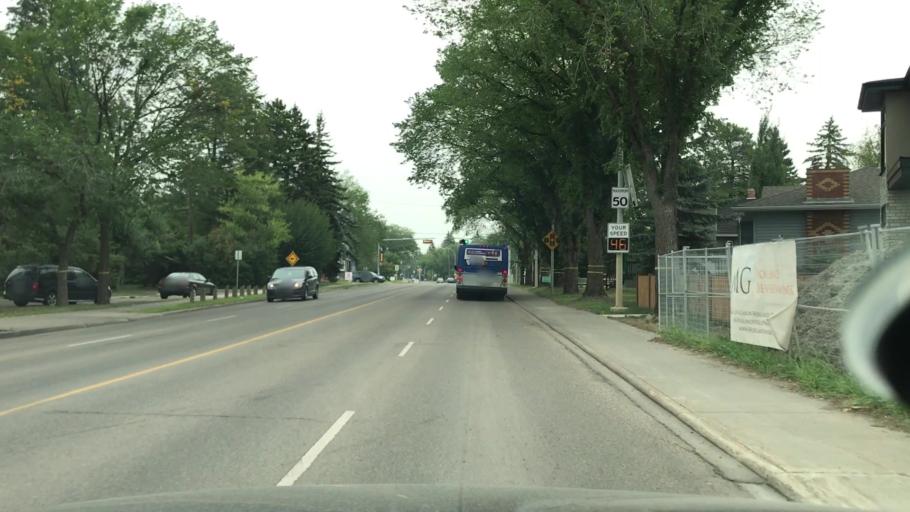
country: CA
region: Alberta
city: Edmonton
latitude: 53.5443
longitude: -113.5580
